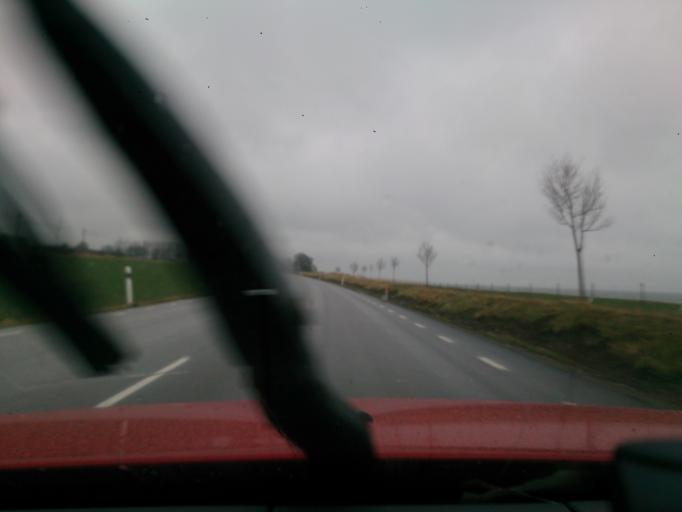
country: SE
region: Skane
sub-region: Ystads Kommun
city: Ystad
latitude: 55.4264
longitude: 13.7298
